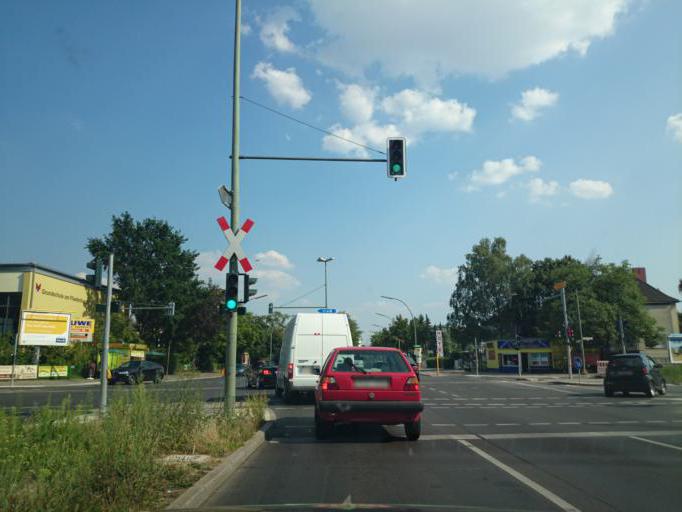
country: DE
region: Berlin
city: Rudow
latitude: 52.4243
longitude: 13.4852
